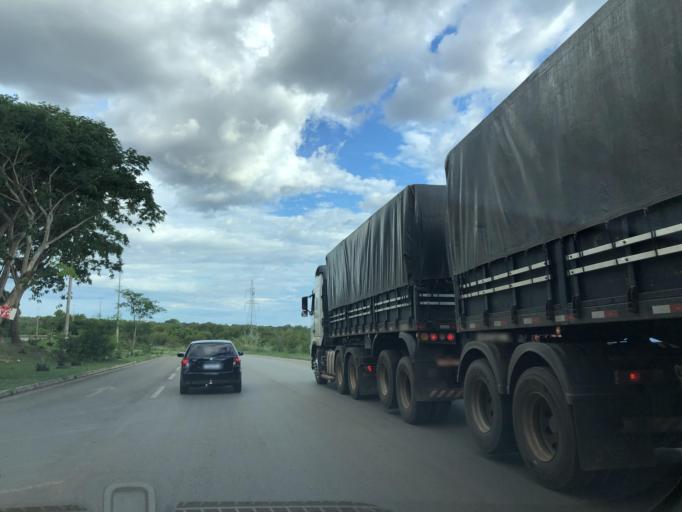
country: BR
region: Goias
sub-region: Luziania
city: Luziania
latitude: -16.0414
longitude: -48.0616
